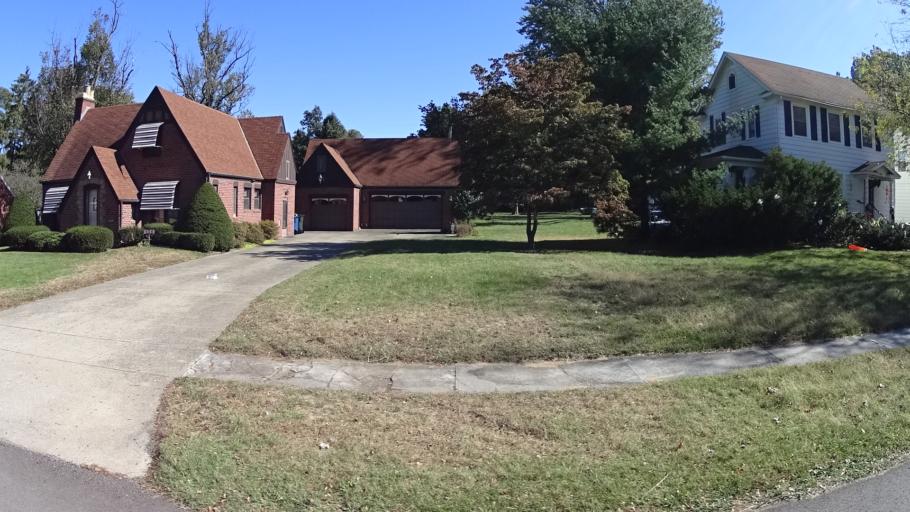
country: US
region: Ohio
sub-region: Lorain County
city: Amherst
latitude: 41.4015
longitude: -82.2155
